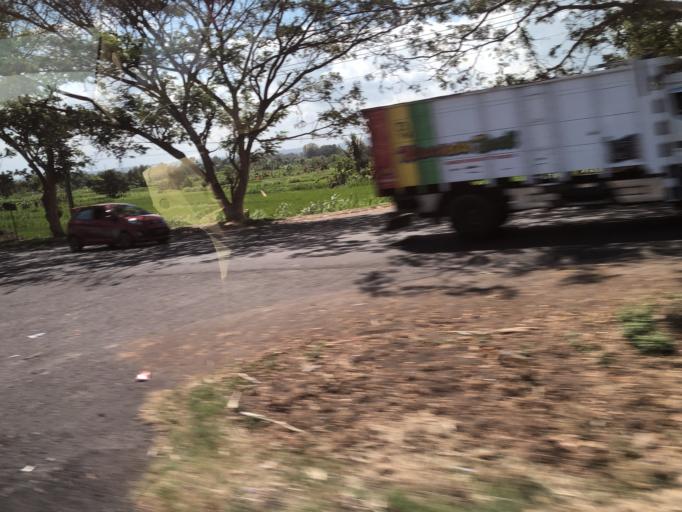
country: ID
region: Bali
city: Semarapura
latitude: -8.5696
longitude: 115.4050
